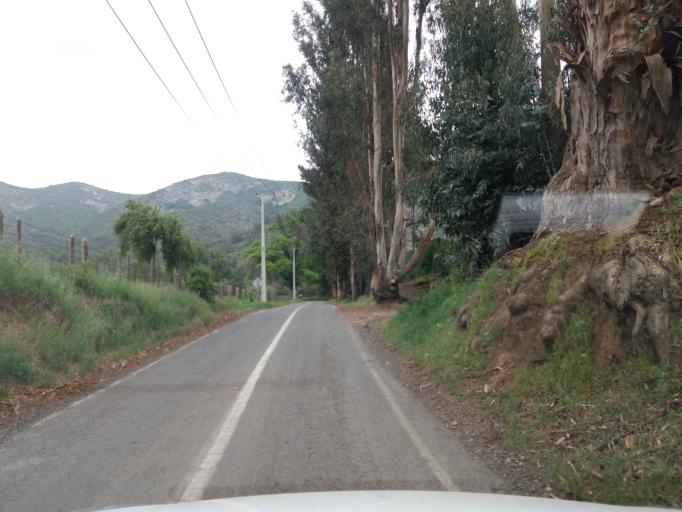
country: CL
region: Valparaiso
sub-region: Provincia de Quillota
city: Quillota
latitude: -32.9076
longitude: -71.1003
